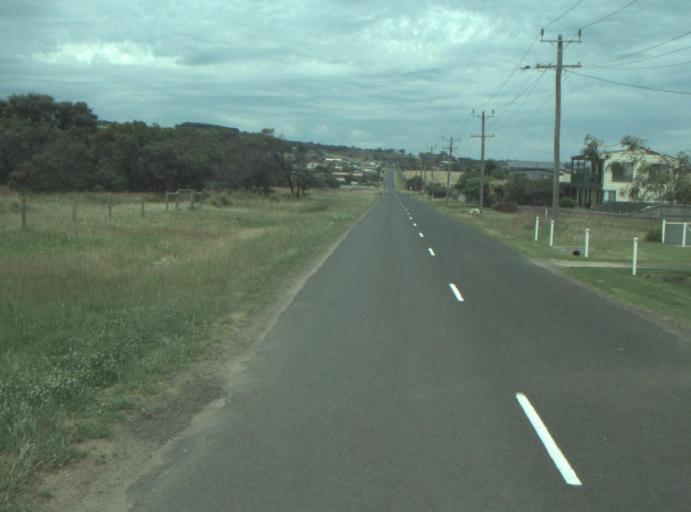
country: AU
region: Victoria
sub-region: Greater Geelong
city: Clifton Springs
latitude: -38.1132
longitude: 144.6292
